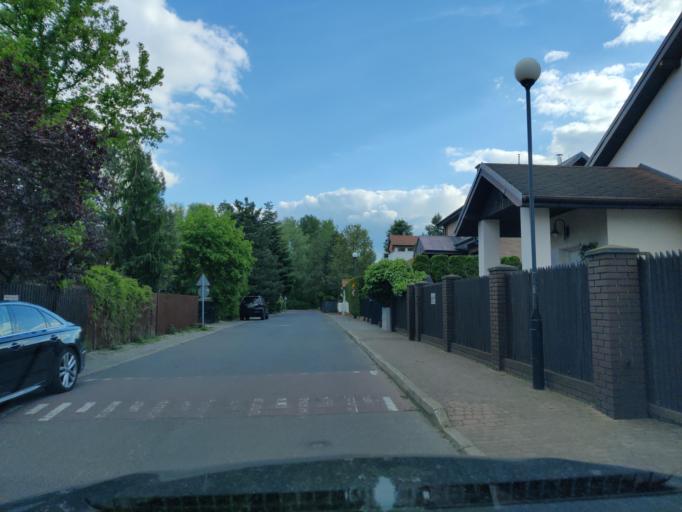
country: PL
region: Masovian Voivodeship
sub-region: Warszawa
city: Kabaty
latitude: 52.1288
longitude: 21.0926
